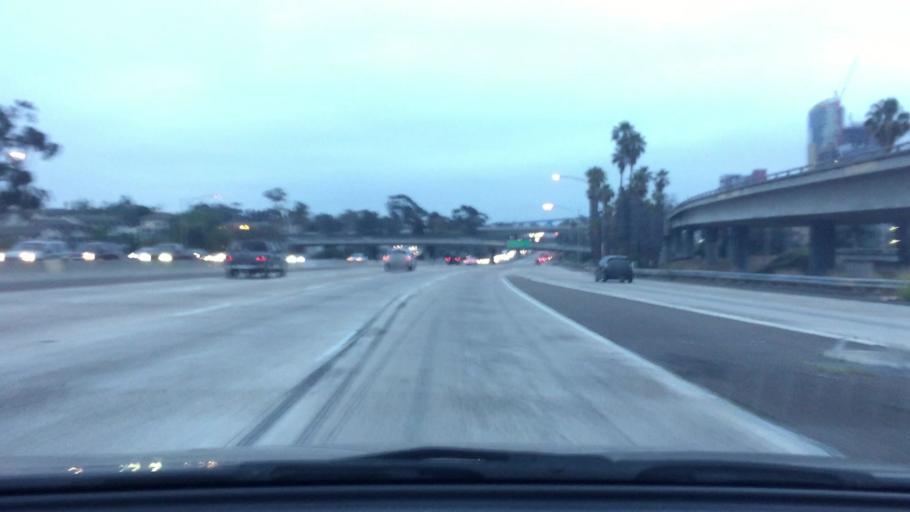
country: US
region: California
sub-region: San Diego County
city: San Diego
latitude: 32.7187
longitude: -117.1480
